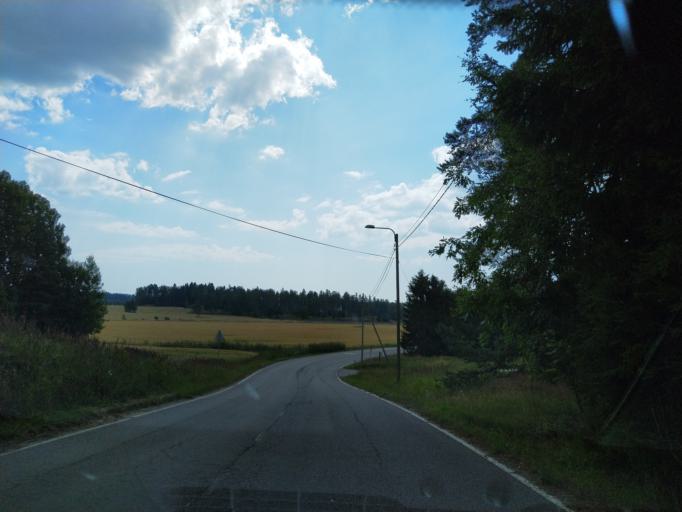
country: FI
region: Uusimaa
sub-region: Helsinki
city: Kirkkonummi
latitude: 60.0510
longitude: 24.5042
